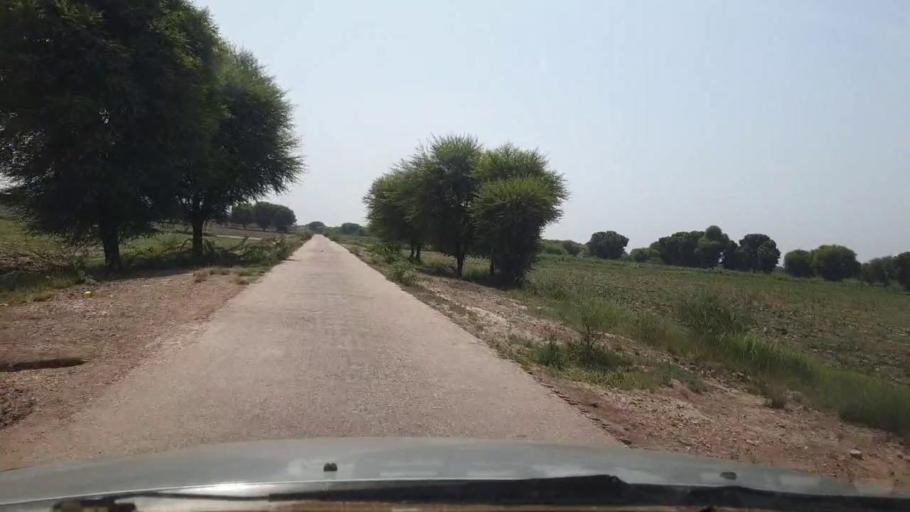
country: PK
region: Sindh
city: Chambar
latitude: 25.2260
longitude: 68.7777
